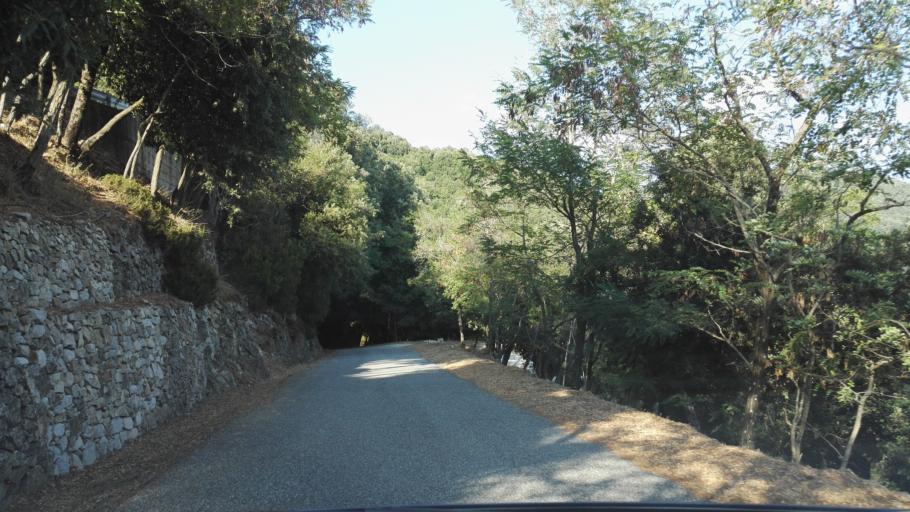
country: IT
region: Calabria
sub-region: Provincia di Vibo-Valentia
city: Nardodipace
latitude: 38.4551
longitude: 16.3461
